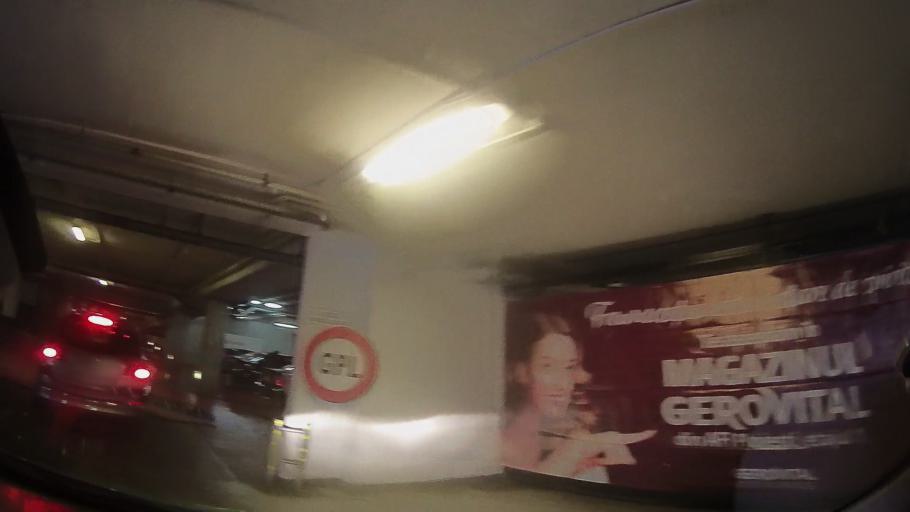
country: RO
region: Prahova
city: Ploiesti
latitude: 44.9474
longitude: 26.0337
